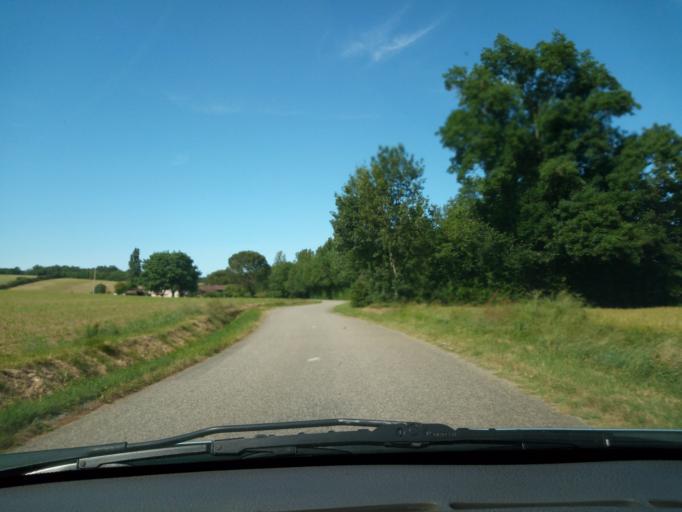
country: FR
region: Midi-Pyrenees
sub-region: Departement du Tarn-et-Garonne
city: Molieres
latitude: 44.2041
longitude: 1.3054
